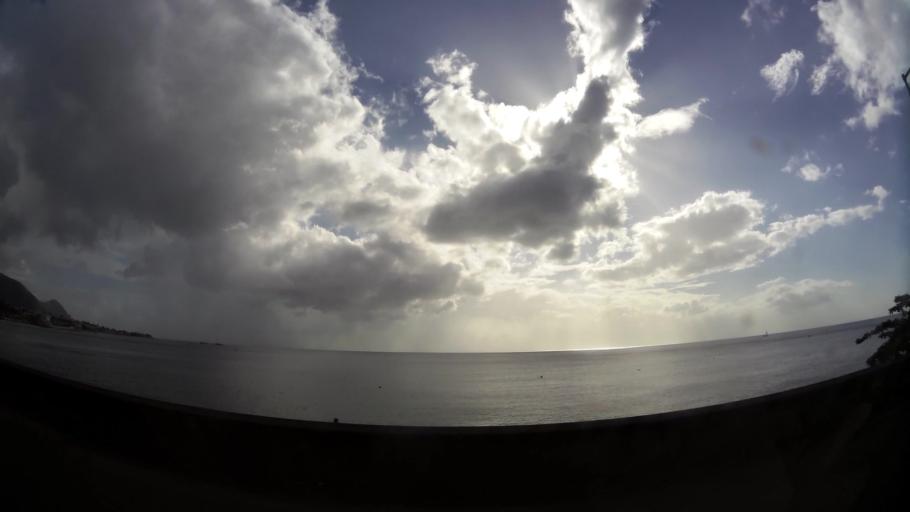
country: DM
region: Saint George
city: Roseau
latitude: 15.3184
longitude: -61.3919
